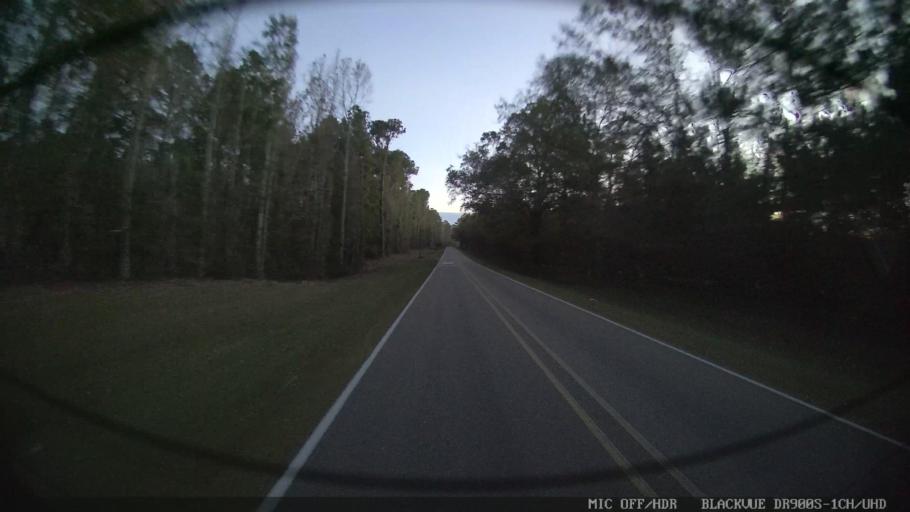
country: US
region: Mississippi
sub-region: Perry County
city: New Augusta
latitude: 31.1319
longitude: -89.1967
